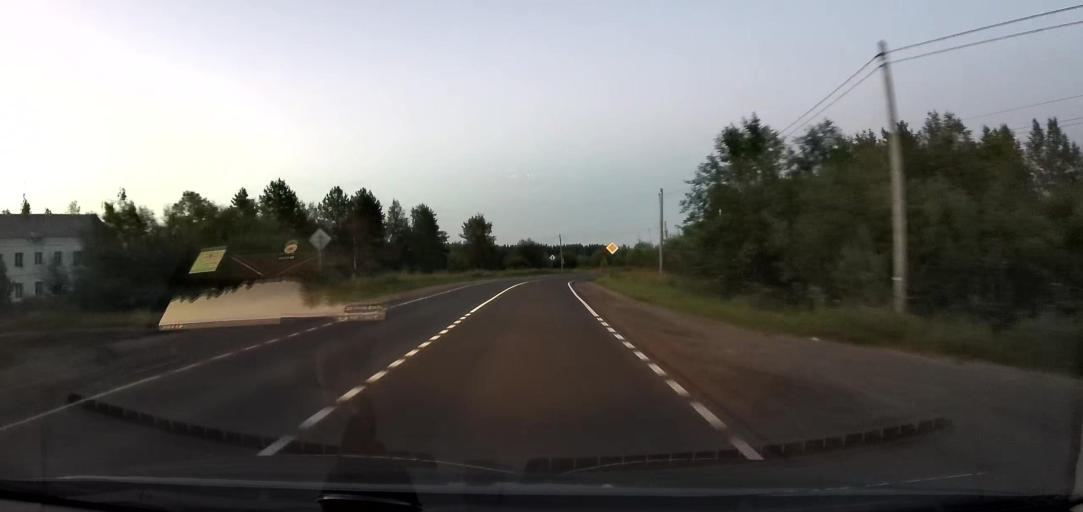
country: RU
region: Arkhangelskaya
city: Uyemskiy
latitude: 64.4411
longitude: 40.9599
